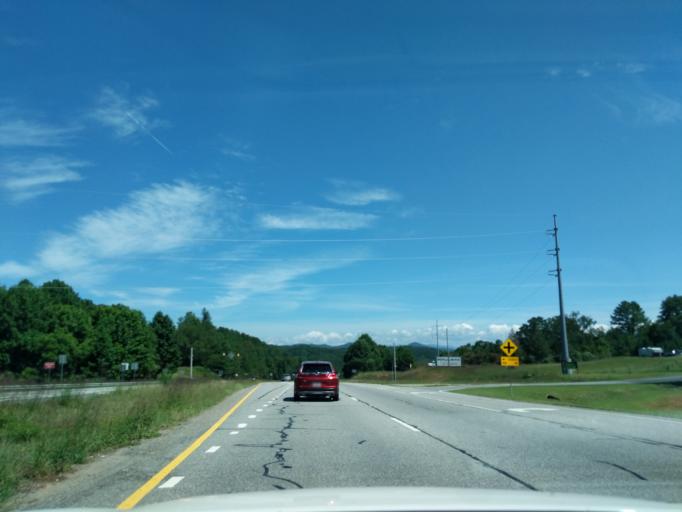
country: US
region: Georgia
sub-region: Fannin County
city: Blue Ridge
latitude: 34.8932
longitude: -84.2605
